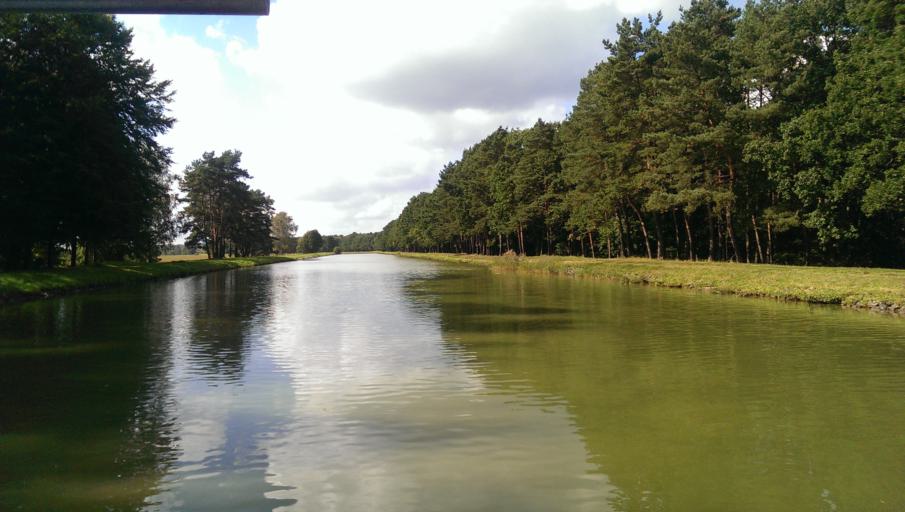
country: DE
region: Brandenburg
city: Melchow
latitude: 52.8604
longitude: 13.7082
